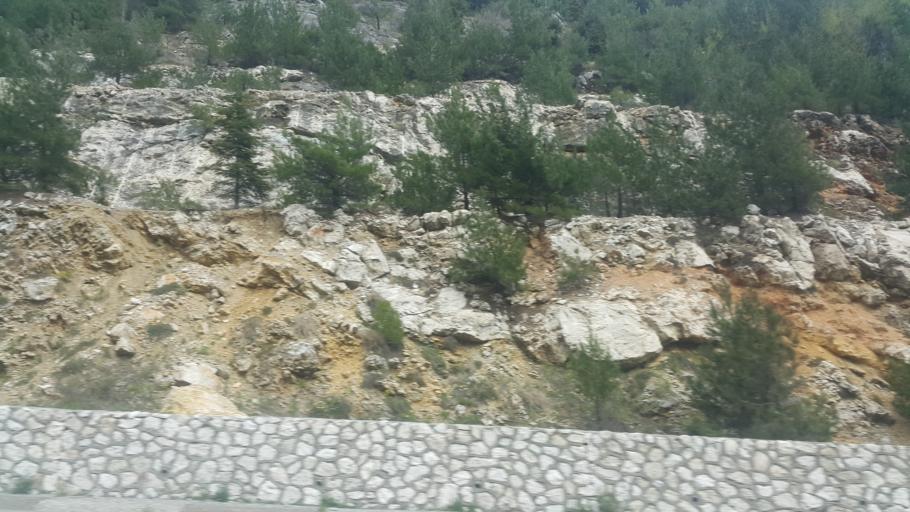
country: TR
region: Adana
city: Pozanti
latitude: 37.2654
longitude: 34.8000
